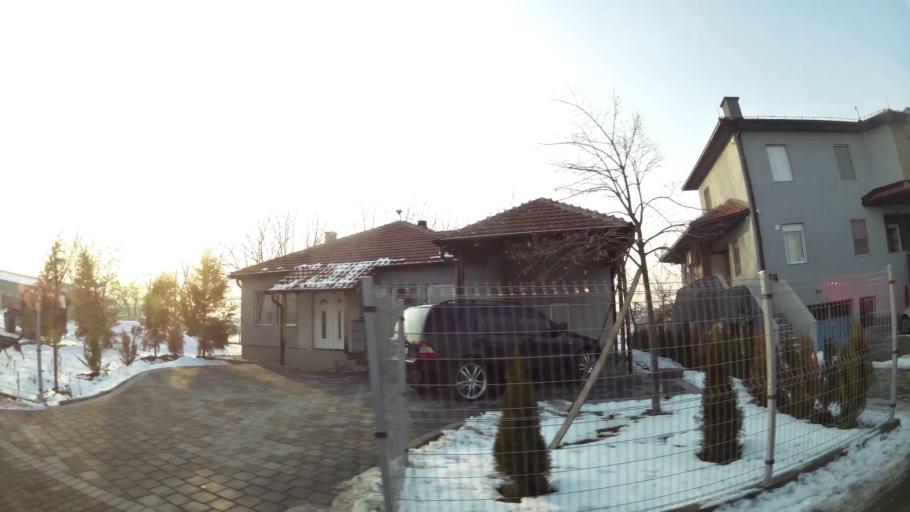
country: MK
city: Creshevo
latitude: 42.0164
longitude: 21.5233
